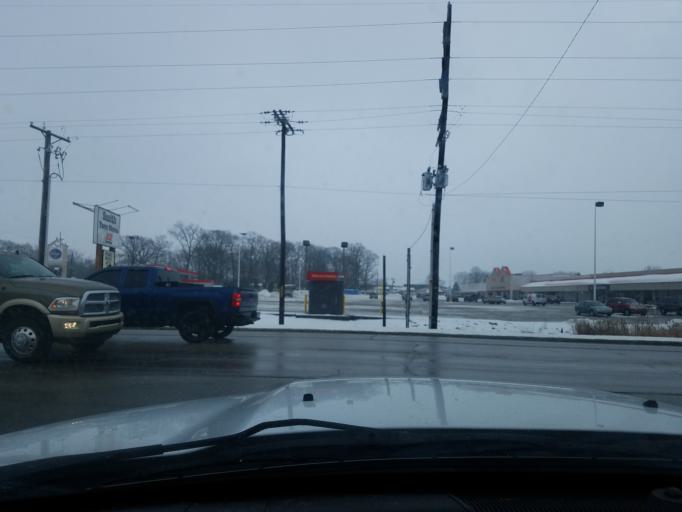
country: US
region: Indiana
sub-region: Fulton County
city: Rochester
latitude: 41.0542
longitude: -86.2178
